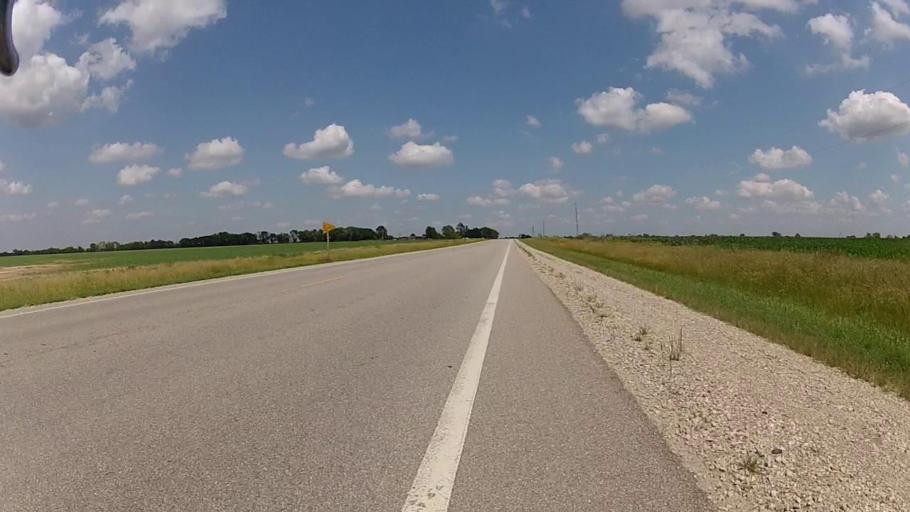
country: US
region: Kansas
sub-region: Labette County
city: Oswego
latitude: 37.1933
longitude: -95.1618
